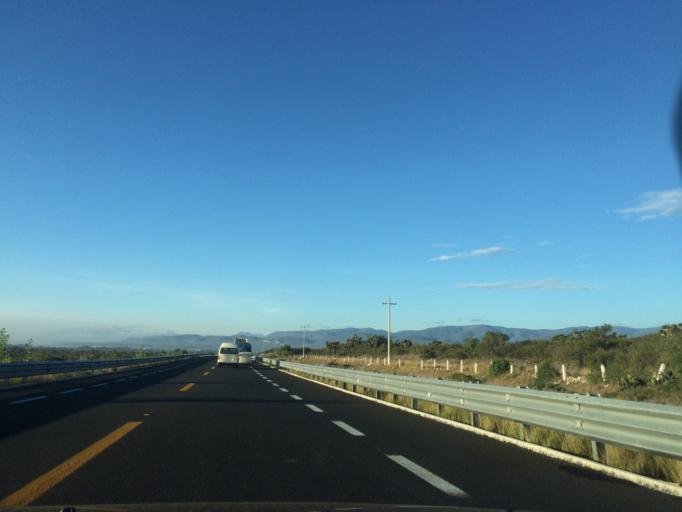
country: MX
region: Puebla
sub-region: Tehuacan
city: Magdalena Cuayucatepec
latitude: 18.5604
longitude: -97.4633
